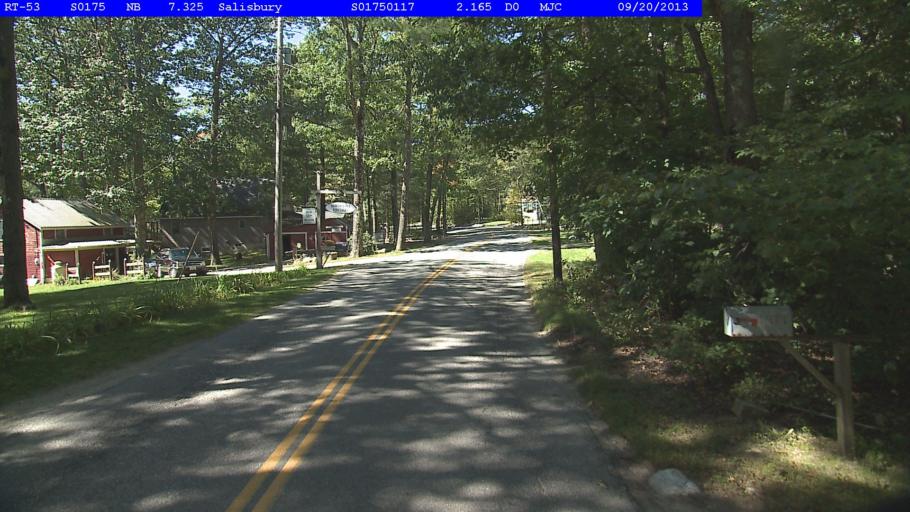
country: US
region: Vermont
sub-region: Rutland County
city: Brandon
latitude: 43.9249
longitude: -73.0792
